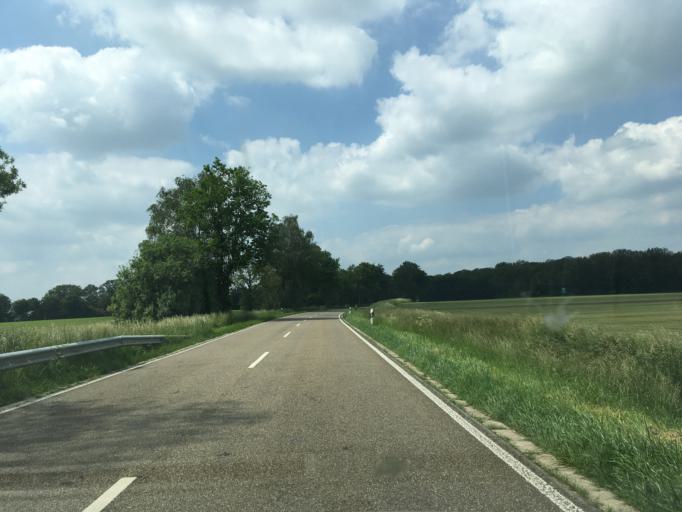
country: DE
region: North Rhine-Westphalia
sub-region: Regierungsbezirk Munster
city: Raesfeld
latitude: 51.7797
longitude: 6.7831
